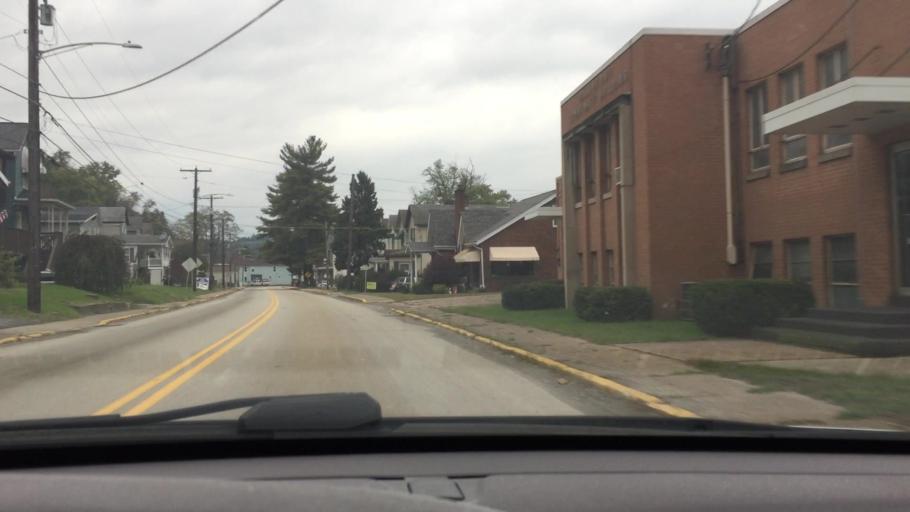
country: US
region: Pennsylvania
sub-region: Fayette County
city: Fairhope
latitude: 40.0966
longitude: -79.8444
